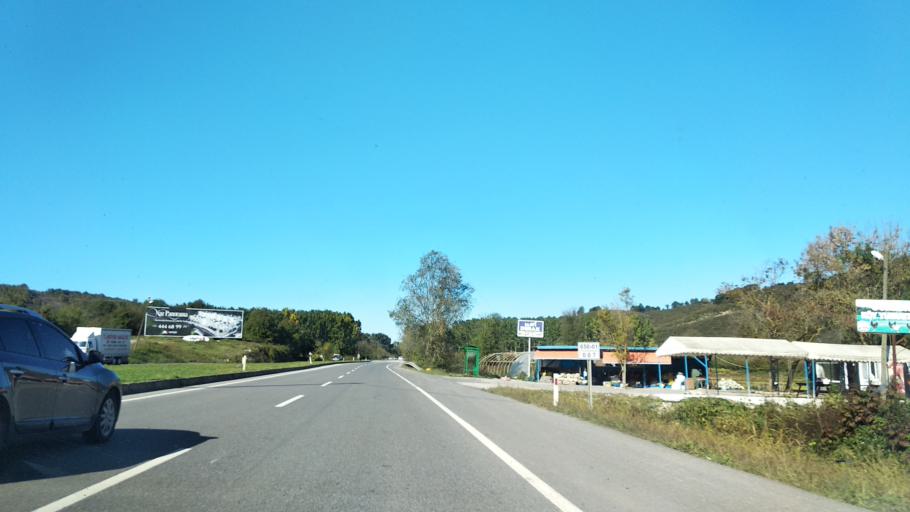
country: TR
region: Sakarya
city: Karasu
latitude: 41.0545
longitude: 30.6357
